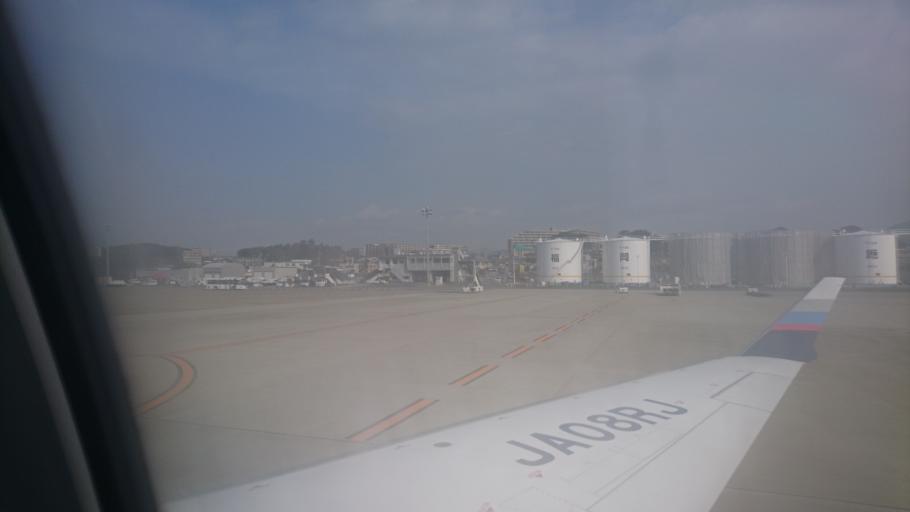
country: JP
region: Fukuoka
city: Fukuoka-shi
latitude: 33.5898
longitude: 130.4503
